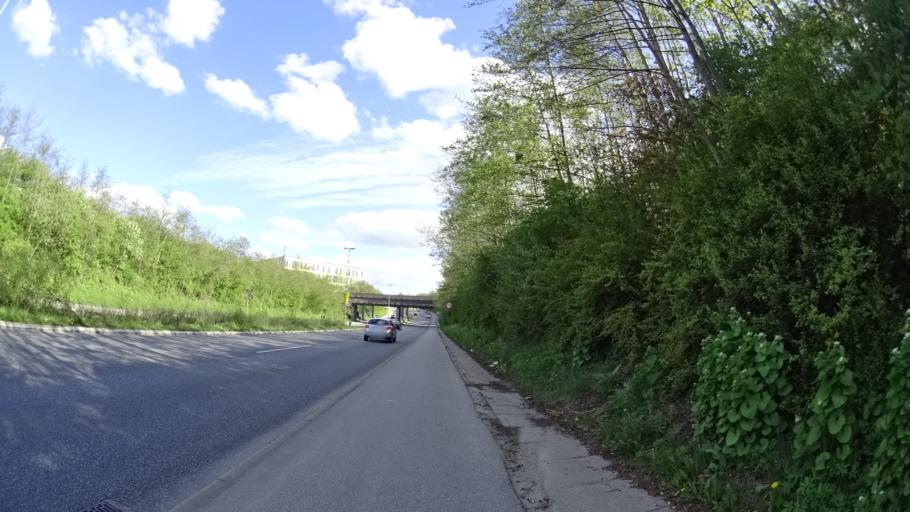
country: DK
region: Central Jutland
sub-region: Arhus Kommune
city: Stavtrup
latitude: 56.1186
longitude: 10.1478
